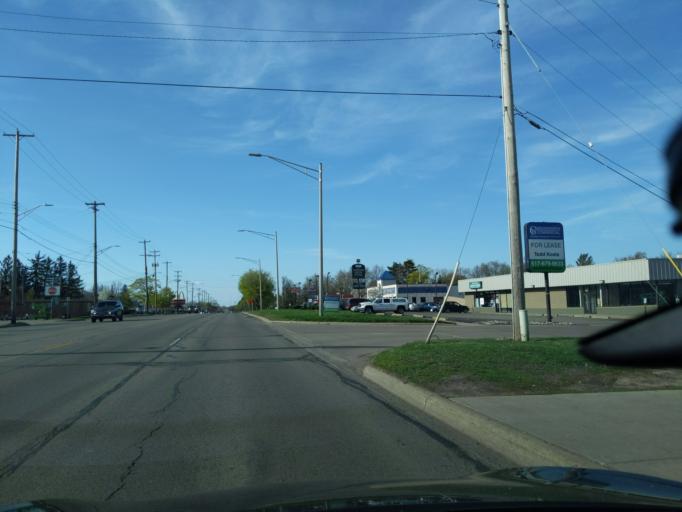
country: US
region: Michigan
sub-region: Ingham County
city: Lansing
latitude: 42.6839
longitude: -84.5480
